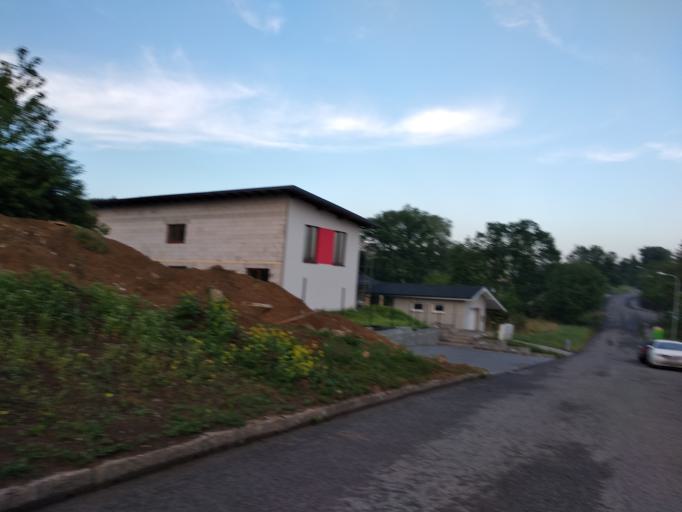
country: CZ
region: Moravskoslezsky
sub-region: Okres Frydek-Mistek
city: Stare Mesto
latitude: 49.6907
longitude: 18.3715
